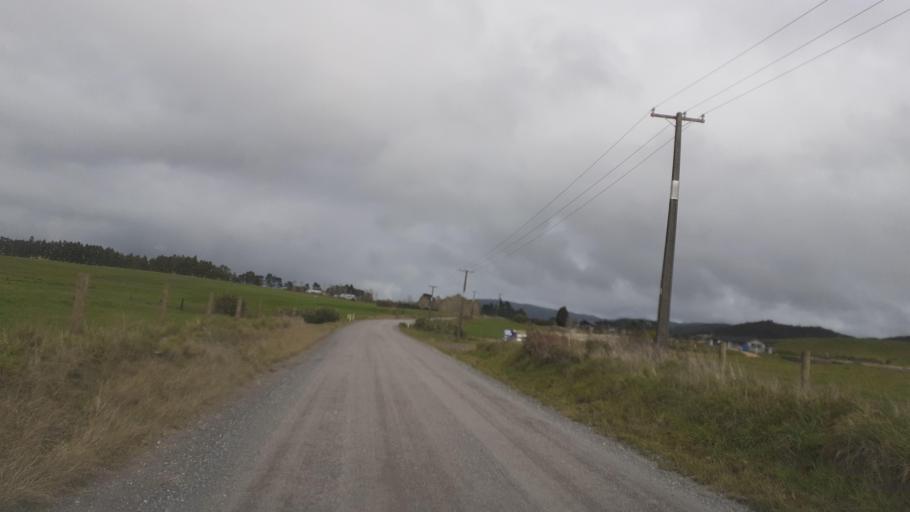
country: NZ
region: Northland
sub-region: Far North District
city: Waimate North
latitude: -35.2436
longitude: 173.8047
